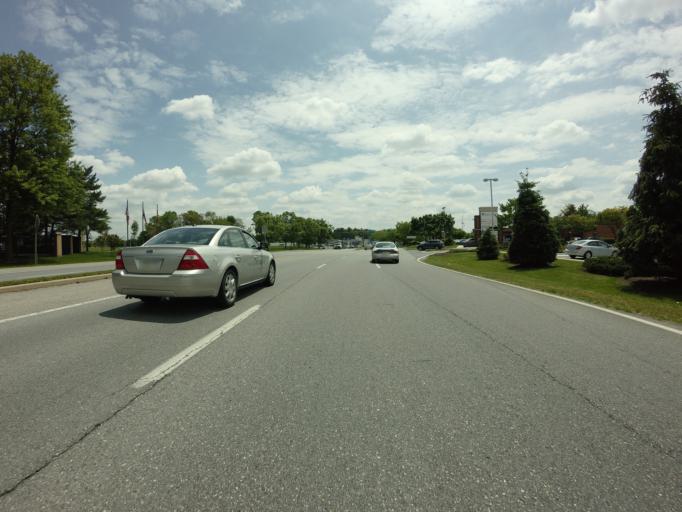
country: US
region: Maryland
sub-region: Frederick County
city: Ballenger Creek
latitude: 39.3767
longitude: -77.4121
